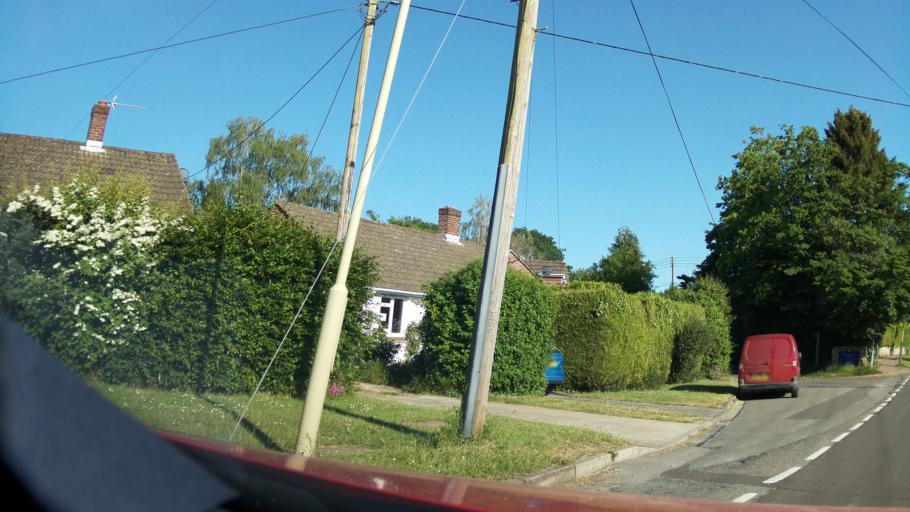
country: GB
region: England
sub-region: Hampshire
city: Compton
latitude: 50.9950
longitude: -1.3509
